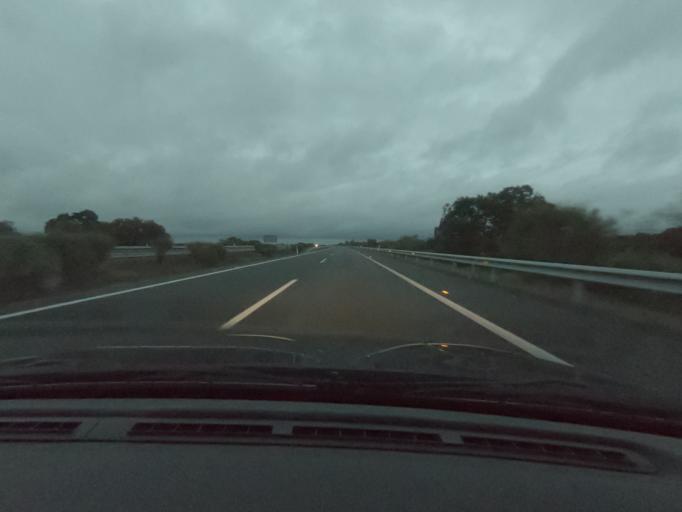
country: ES
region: Extremadura
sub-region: Provincia de Caceres
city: Casas de Don Antonio
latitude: 39.2413
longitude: -6.3044
